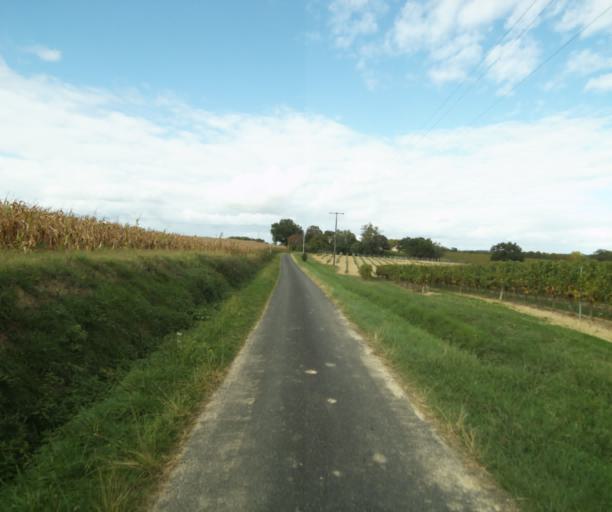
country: FR
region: Midi-Pyrenees
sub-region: Departement du Gers
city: Eauze
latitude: 43.9278
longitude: 0.1178
